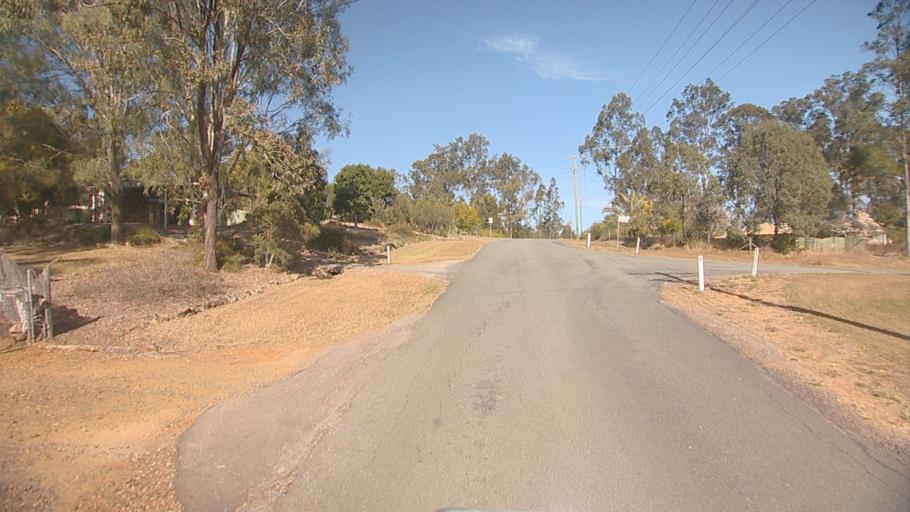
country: AU
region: Queensland
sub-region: Logan
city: Cedar Vale
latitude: -27.8543
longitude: 152.9857
